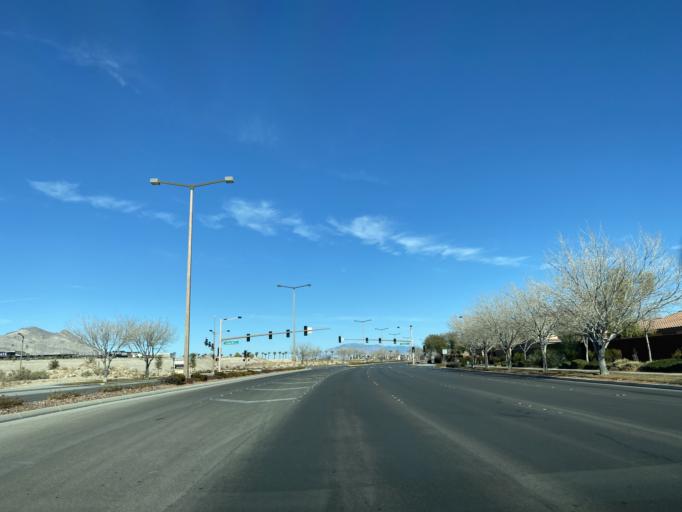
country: US
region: Nevada
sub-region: Clark County
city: Summerlin South
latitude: 36.1458
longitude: -115.3263
